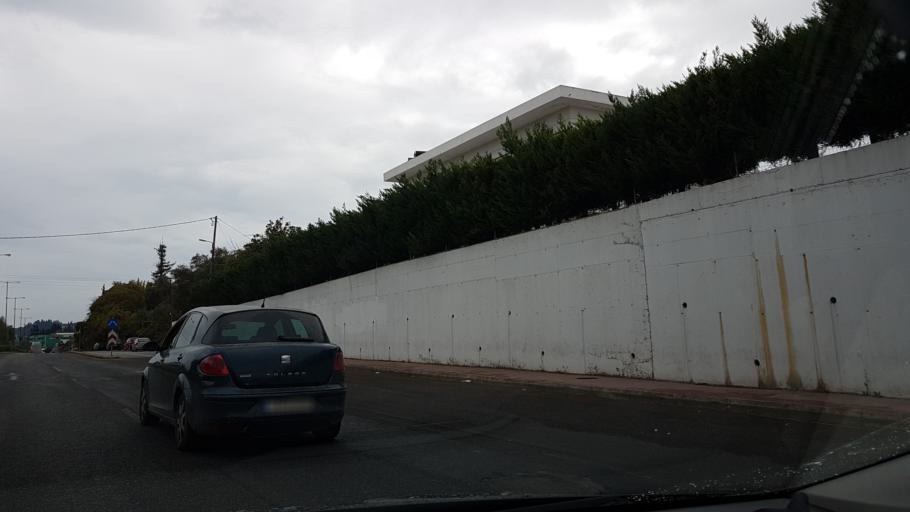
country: GR
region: Ionian Islands
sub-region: Nomos Kerkyras
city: Kontokali
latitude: 39.6570
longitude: 19.8394
